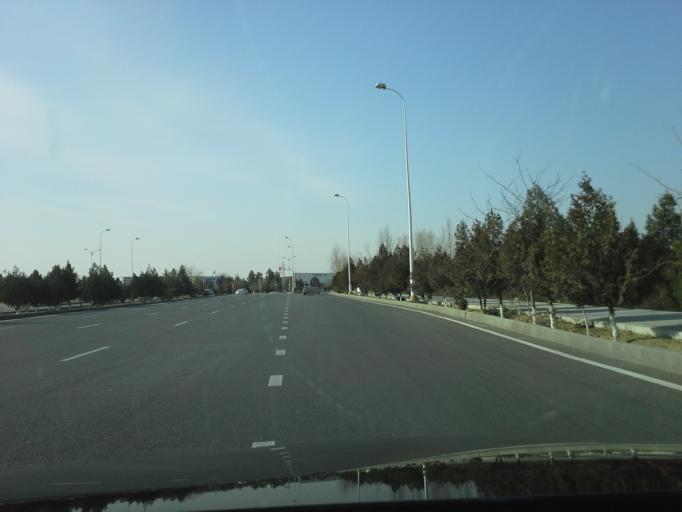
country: TM
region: Ahal
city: Abadan
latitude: 38.0511
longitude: 58.1867
